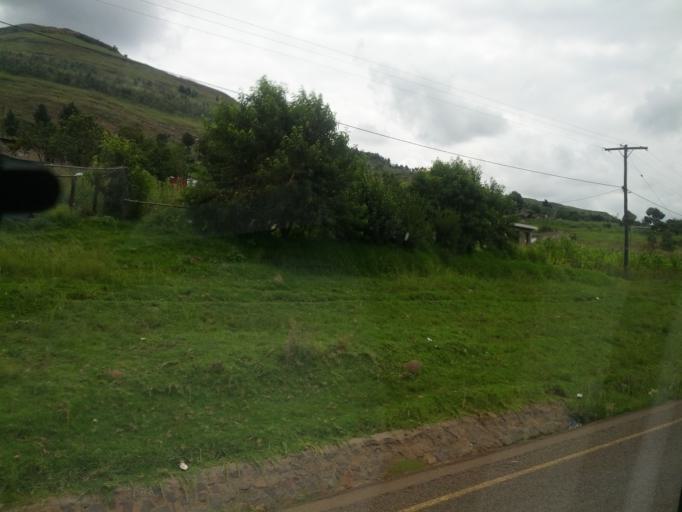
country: LS
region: Leribe
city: Leribe
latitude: -29.0306
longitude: 28.2354
